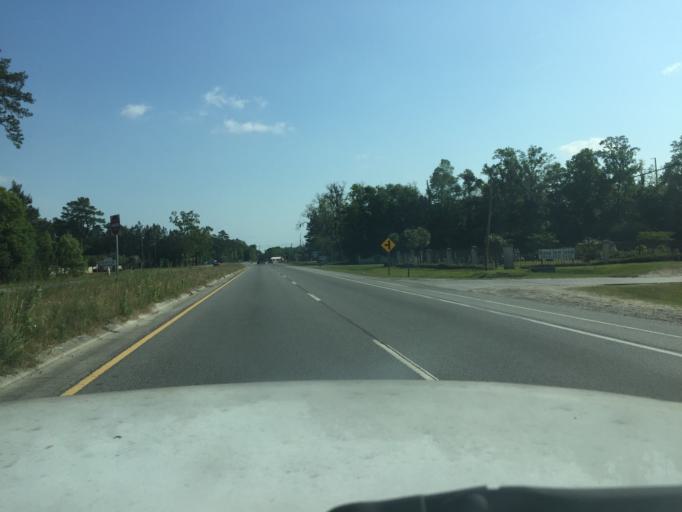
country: US
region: Georgia
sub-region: Chatham County
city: Georgetown
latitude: 32.0320
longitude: -81.2194
